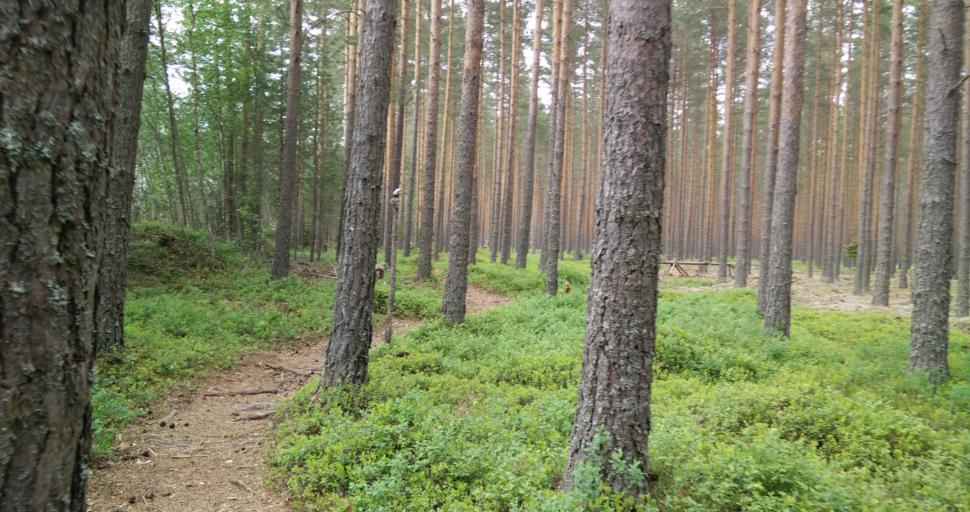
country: SE
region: Vaermland
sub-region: Hagfors Kommun
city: Hagfors
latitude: 60.0143
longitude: 13.5839
